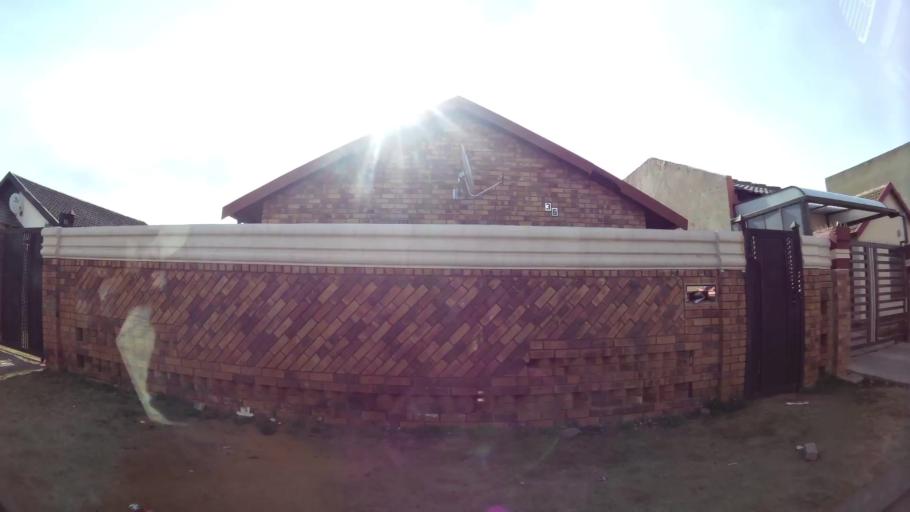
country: ZA
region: Gauteng
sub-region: City of Johannesburg Metropolitan Municipality
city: Roodepoort
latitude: -26.2130
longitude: 27.8633
